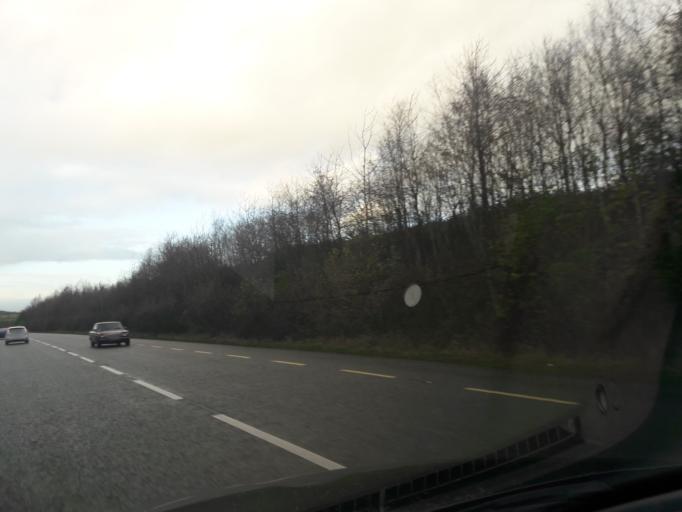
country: IE
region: Leinster
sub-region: Lu
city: Ardee
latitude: 53.9127
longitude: -6.6227
